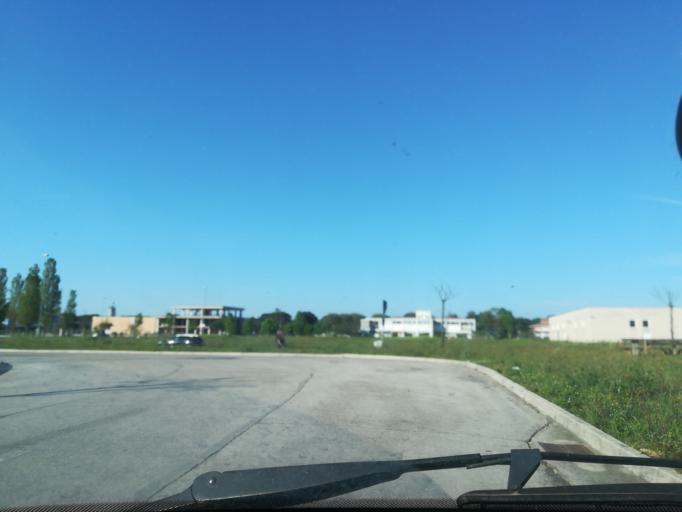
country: IT
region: The Marches
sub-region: Provincia di Macerata
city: Zona Industriale
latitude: 43.2582
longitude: 13.4880
